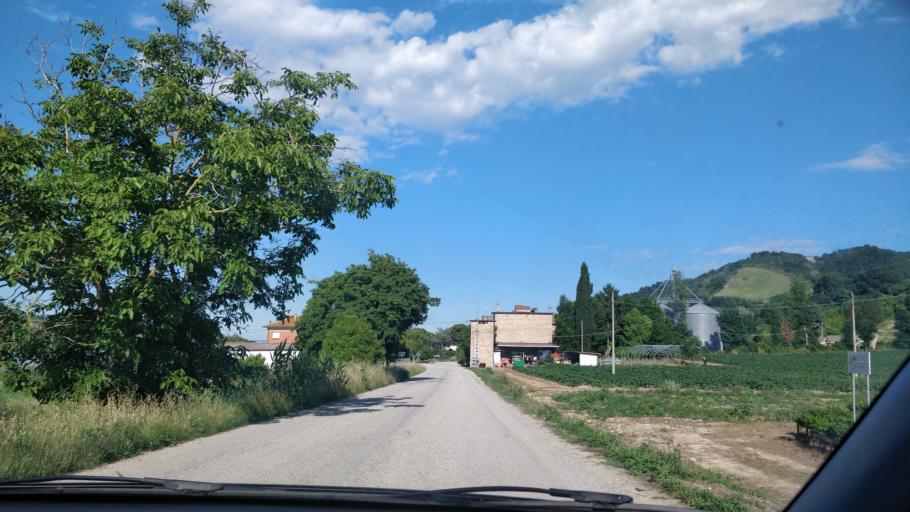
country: IT
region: The Marches
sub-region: Provincia di Ascoli Piceno
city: Massignano
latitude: 43.0337
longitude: 13.7987
